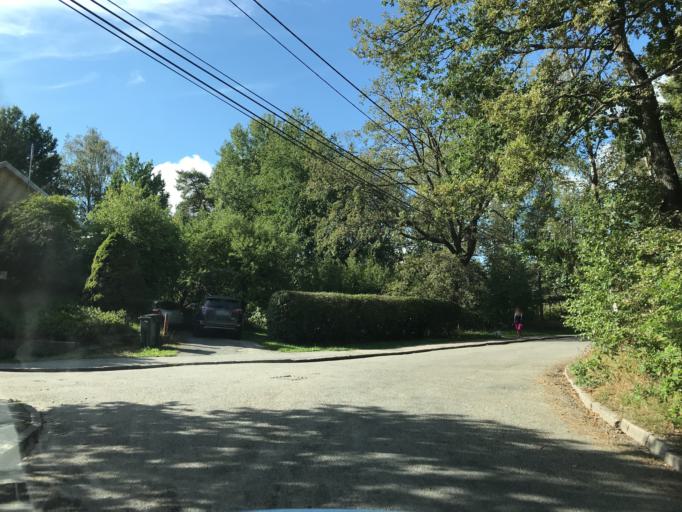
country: SE
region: Stockholm
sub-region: Huddinge Kommun
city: Segeltorp
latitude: 59.2758
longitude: 17.9705
